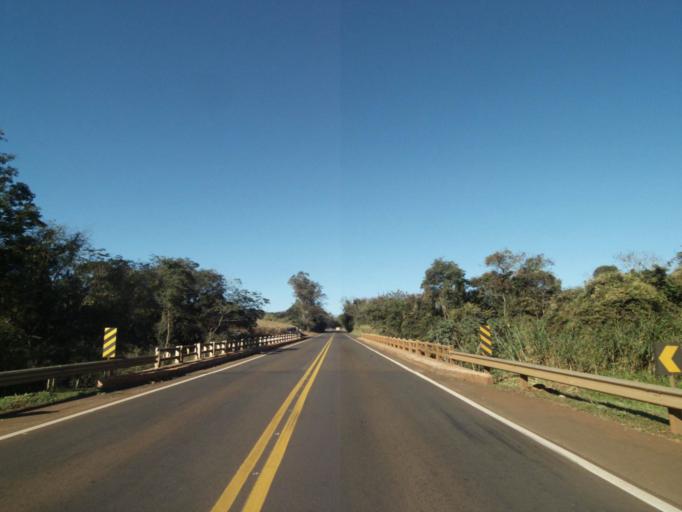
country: BR
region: Parana
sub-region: Londrina
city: Londrina
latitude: -23.4631
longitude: -51.1335
